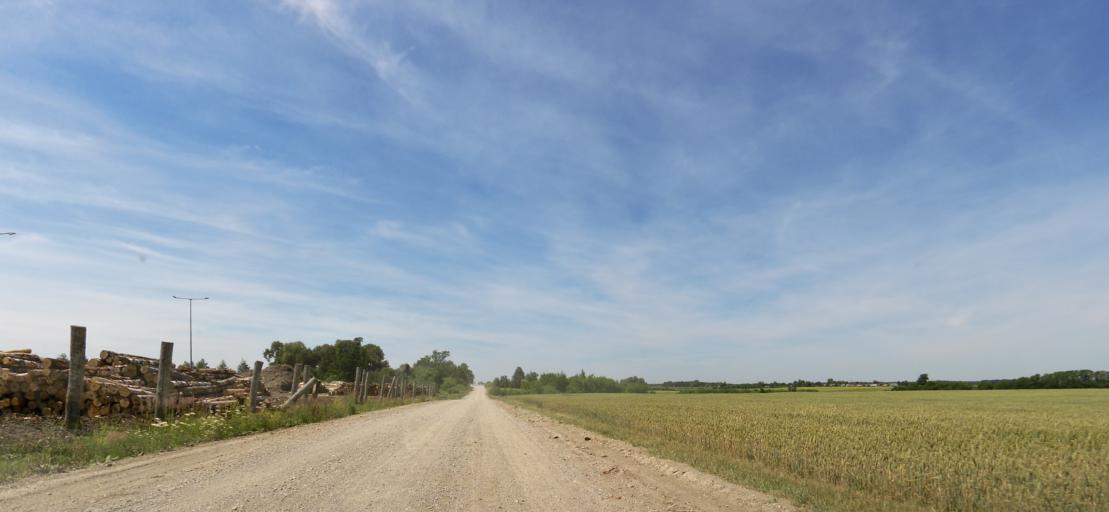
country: LT
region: Vilnius County
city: Ukmerge
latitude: 55.3021
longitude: 24.8084
